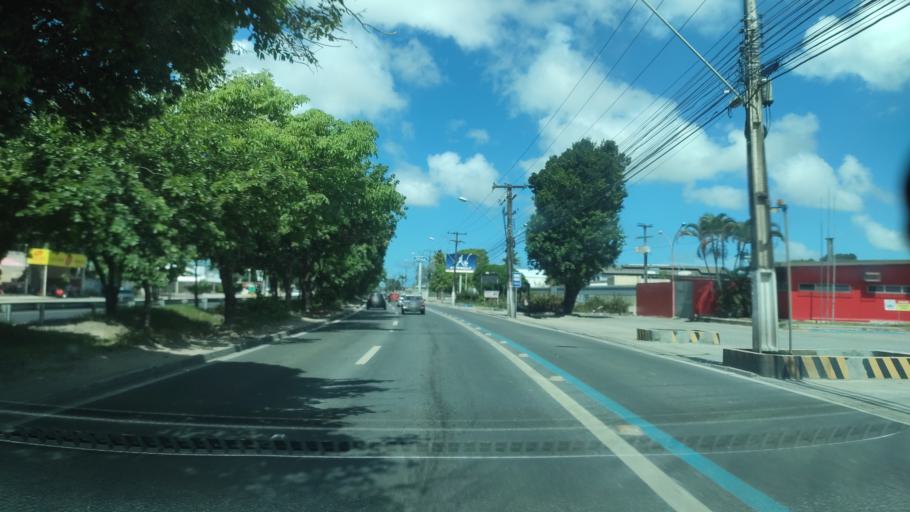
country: BR
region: Alagoas
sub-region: Satuba
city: Satuba
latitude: -9.5904
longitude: -35.7599
